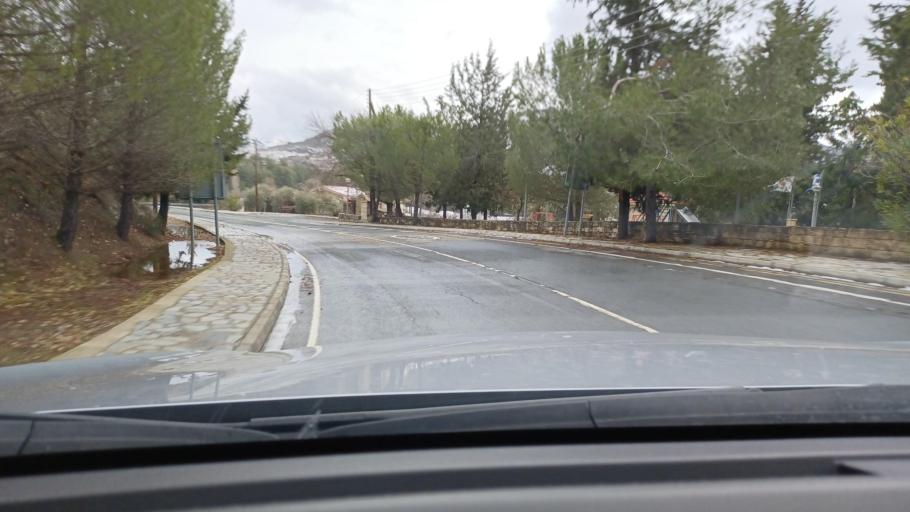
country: CY
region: Limassol
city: Pachna
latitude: 34.8705
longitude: 32.8348
